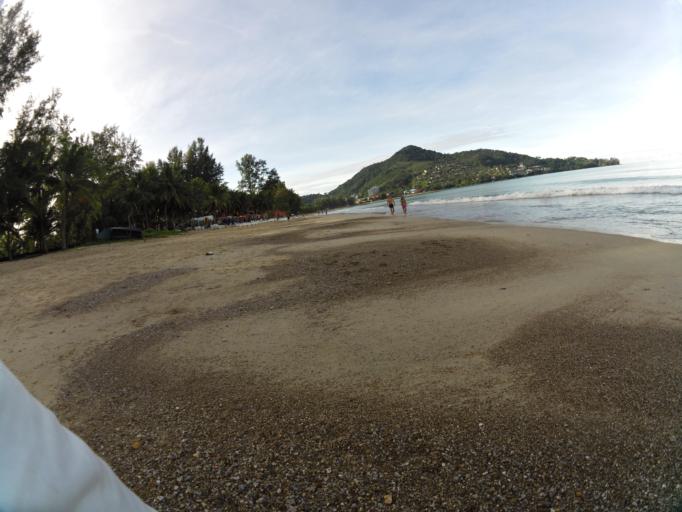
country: TH
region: Phuket
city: Patong
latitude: 7.9577
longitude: 98.2832
